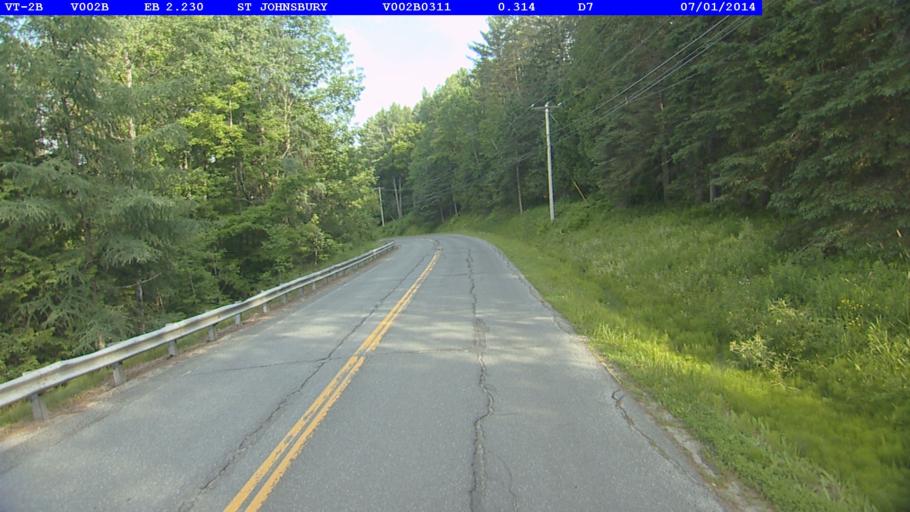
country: US
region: Vermont
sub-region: Caledonia County
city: St Johnsbury
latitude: 44.4276
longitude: -72.0503
